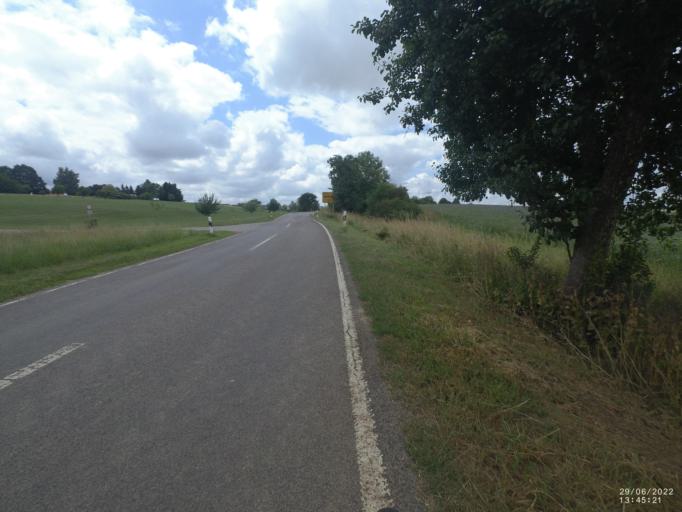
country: DE
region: Baden-Wuerttemberg
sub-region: Regierungsbezirk Stuttgart
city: Bohmenkirch
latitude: 48.6486
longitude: 9.9661
